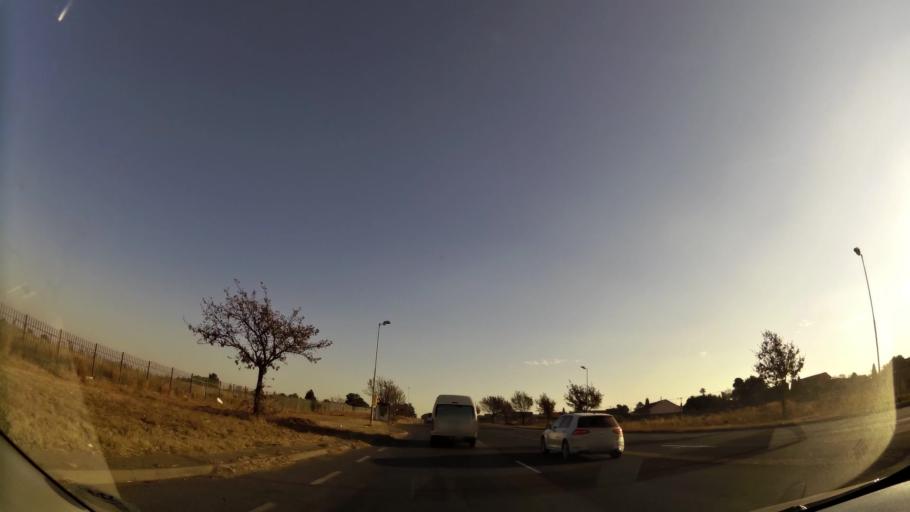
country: ZA
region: Gauteng
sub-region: West Rand District Municipality
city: Randfontein
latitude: -26.2068
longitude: 27.6602
